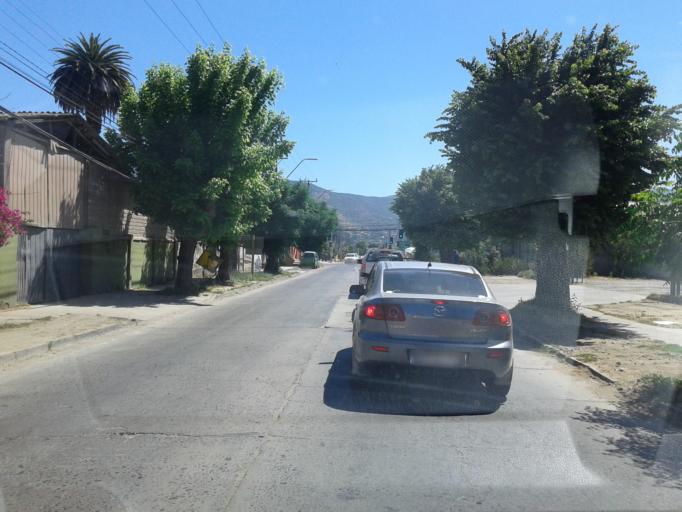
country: CL
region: Valparaiso
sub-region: Provincia de Marga Marga
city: Limache
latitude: -33.0090
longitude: -71.2509
